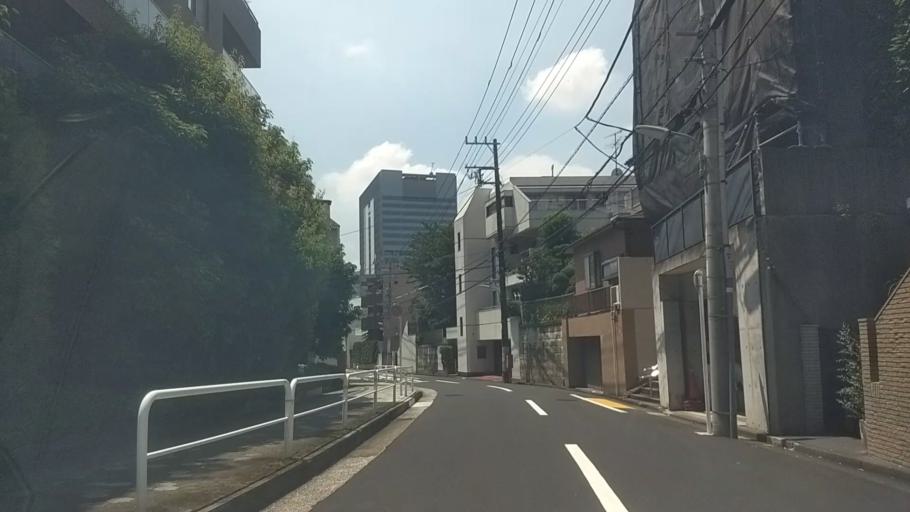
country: JP
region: Tokyo
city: Tokyo
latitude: 35.6281
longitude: 139.7309
